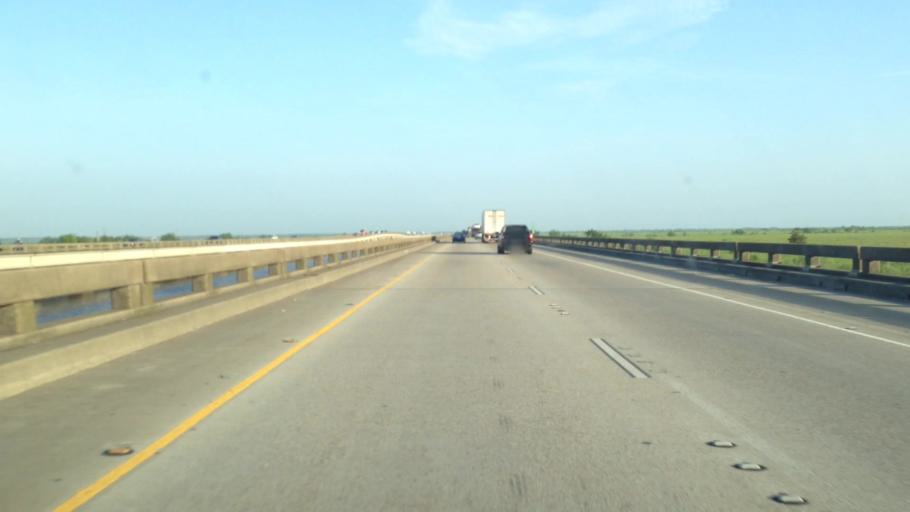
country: US
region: Louisiana
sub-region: Saint Charles Parish
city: Saint Rose
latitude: 30.0240
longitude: -90.3246
